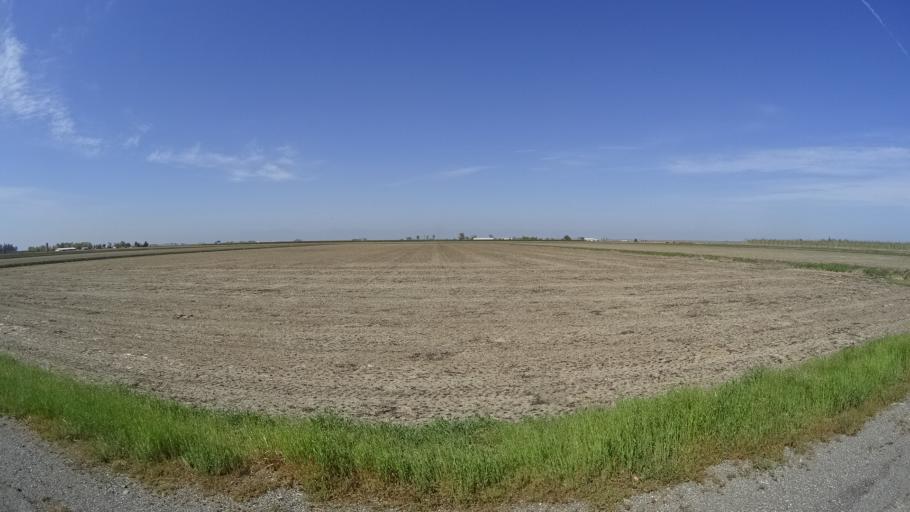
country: US
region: California
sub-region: Glenn County
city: Hamilton City
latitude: 39.6133
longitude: -122.0462
